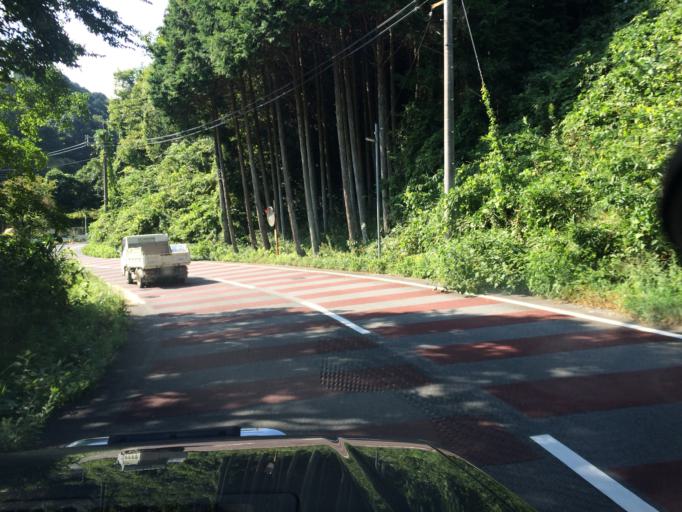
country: JP
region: Mie
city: Nabari
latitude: 34.6972
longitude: 135.9735
